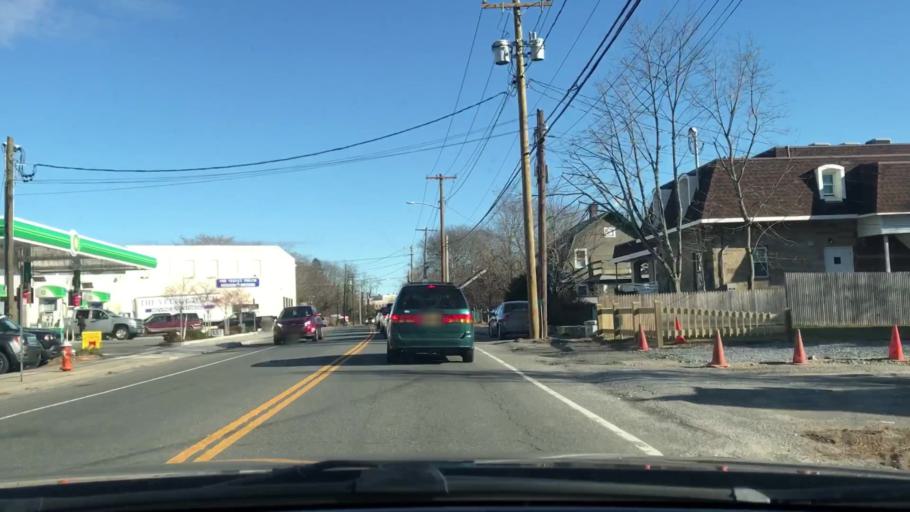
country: US
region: New York
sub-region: Suffolk County
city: Riverhead
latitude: 40.9180
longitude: -72.6735
